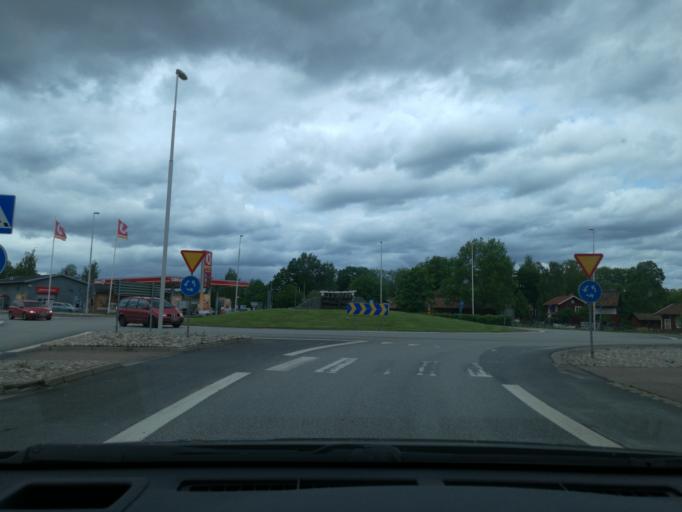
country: SE
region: Vaestmanland
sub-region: Fagersta Kommun
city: Fagersta
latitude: 59.9834
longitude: 15.8085
